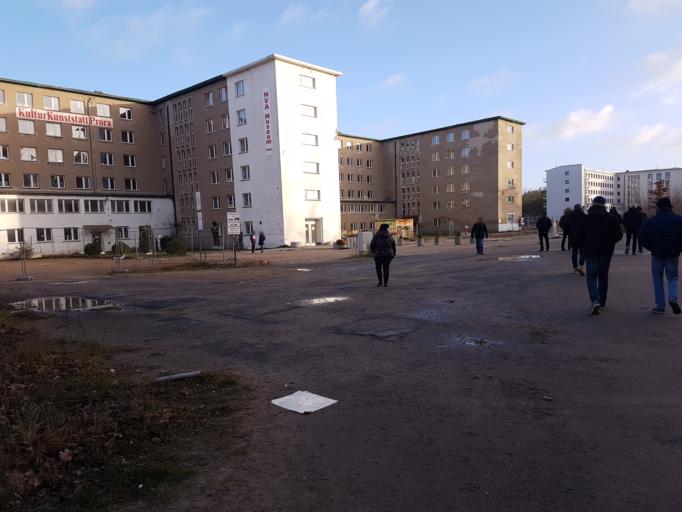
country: DE
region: Mecklenburg-Vorpommern
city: Ostseebad Binz
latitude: 54.4360
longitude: 13.5764
